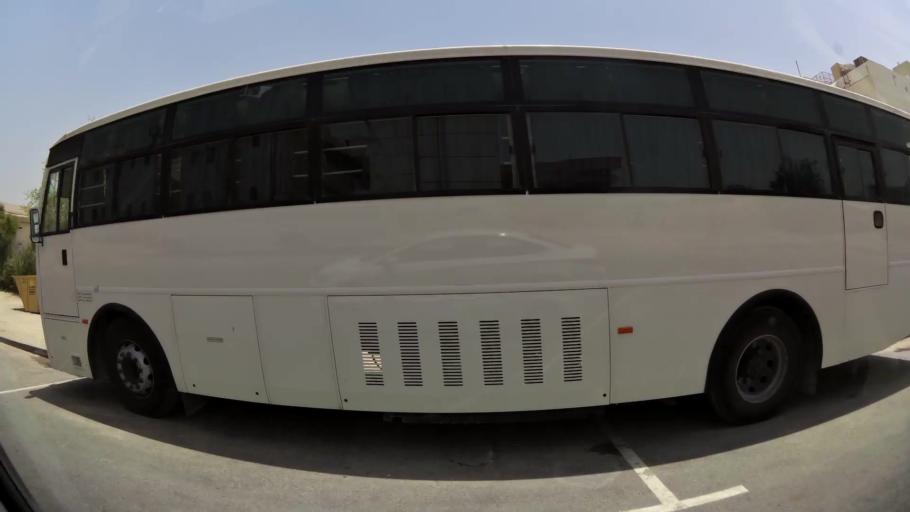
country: AE
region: Ash Shariqah
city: Sharjah
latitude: 25.2734
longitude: 55.4295
